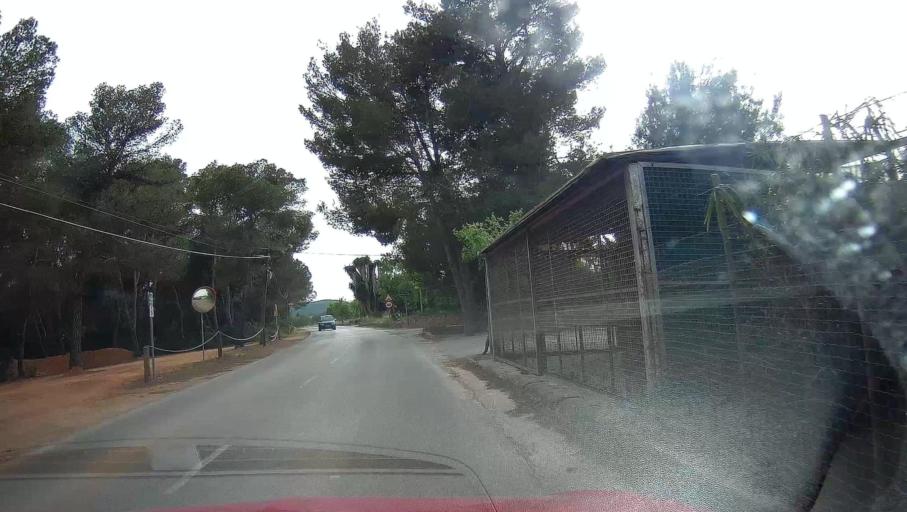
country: ES
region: Balearic Islands
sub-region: Illes Balears
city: Sant Joan de Labritja
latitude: 39.0370
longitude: 1.5412
